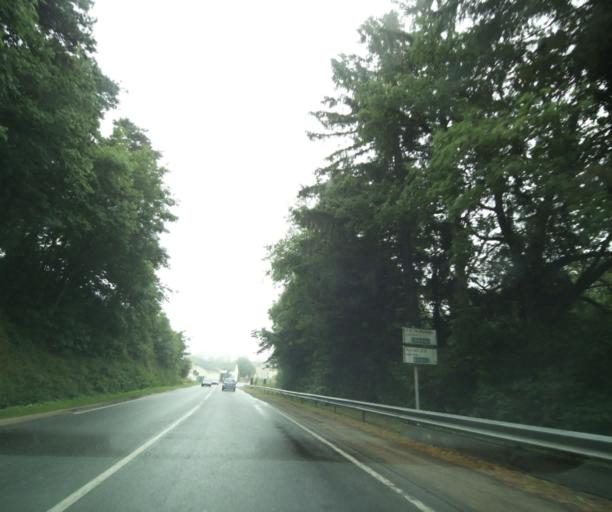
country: FR
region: Midi-Pyrenees
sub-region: Departement de l'Aveyron
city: Baraqueville
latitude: 44.2737
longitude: 2.4288
